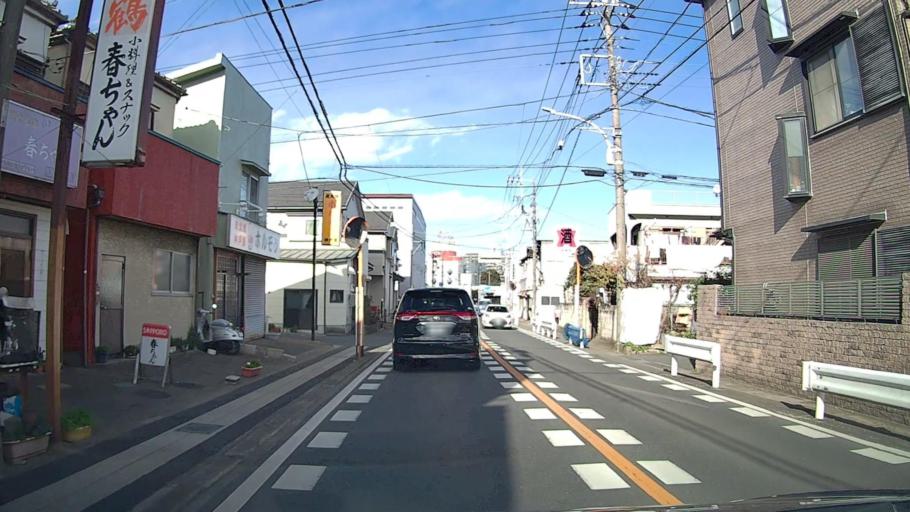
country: JP
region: Saitama
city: Asaka
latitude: 35.7920
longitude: 139.5759
